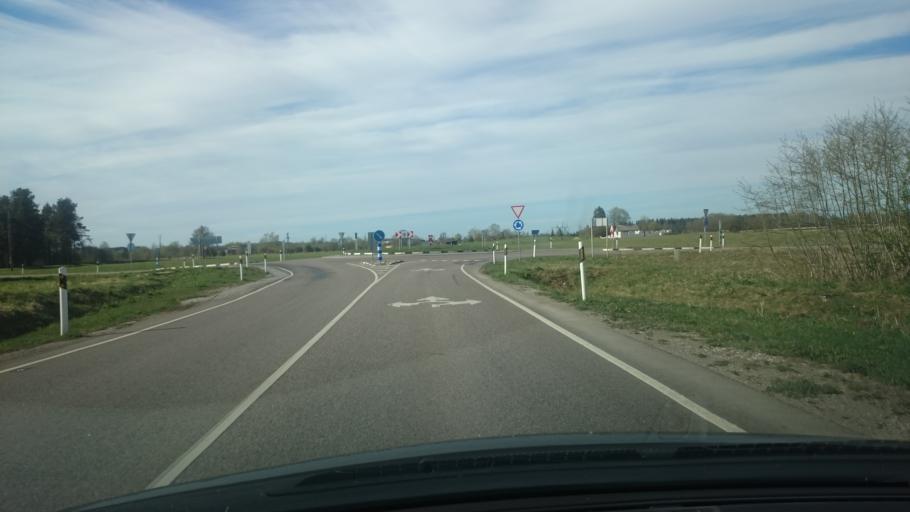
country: EE
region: Ida-Virumaa
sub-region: Johvi vald
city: Johvi
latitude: 59.2938
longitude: 27.4954
